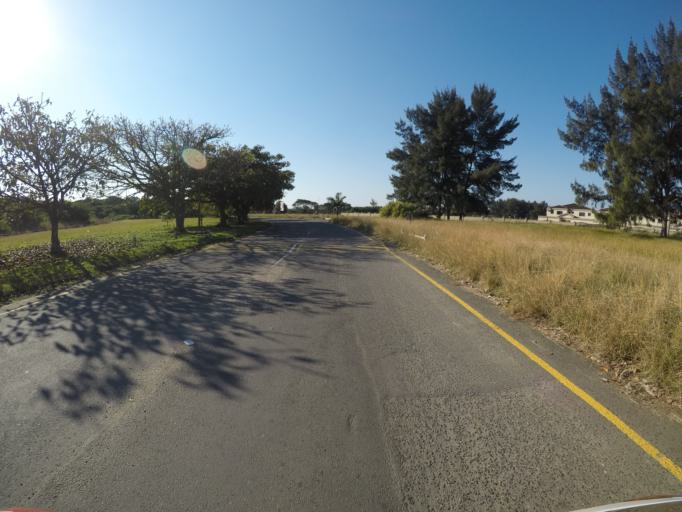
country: ZA
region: KwaZulu-Natal
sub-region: uThungulu District Municipality
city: Richards Bay
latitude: -28.7881
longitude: 32.0796
